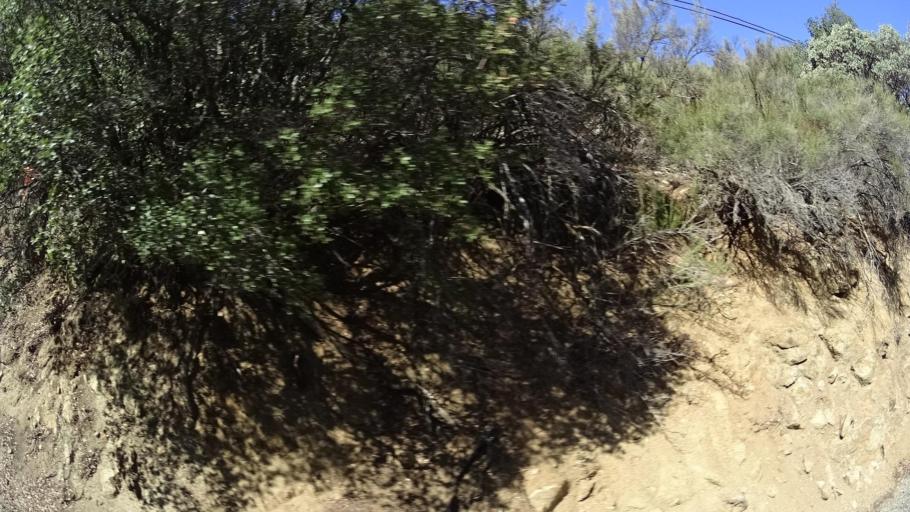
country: US
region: California
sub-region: Riverside County
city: Aguanga
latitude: 33.3194
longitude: -116.6982
